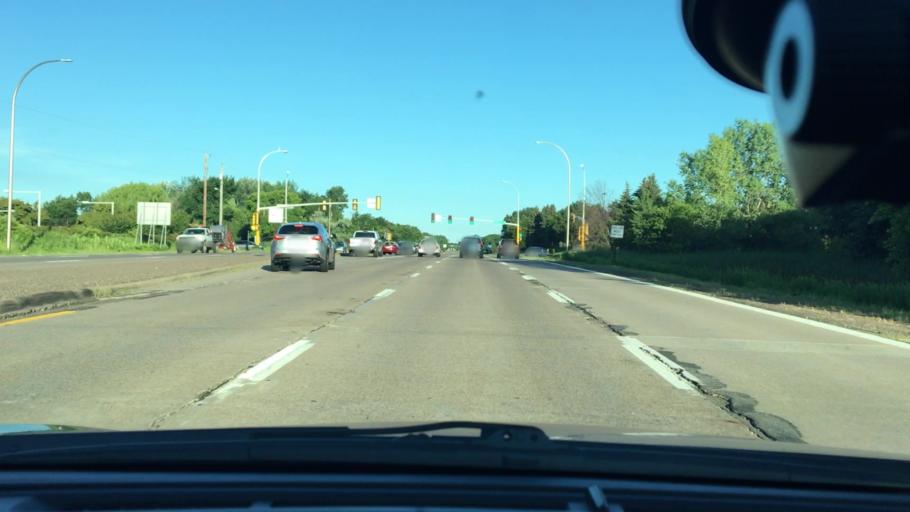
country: US
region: Minnesota
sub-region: Hennepin County
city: New Hope
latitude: 45.0585
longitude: -93.4067
